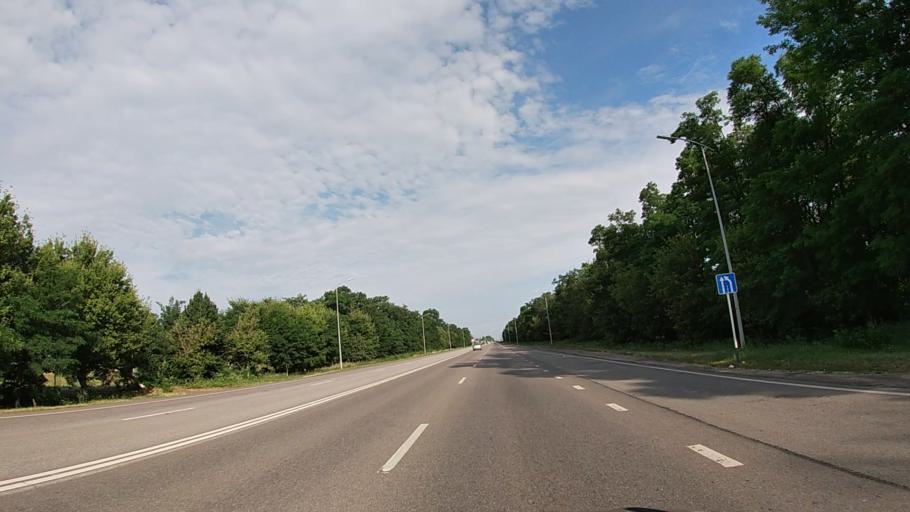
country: RU
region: Belgorod
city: Severnyy
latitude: 50.6392
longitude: 36.4414
